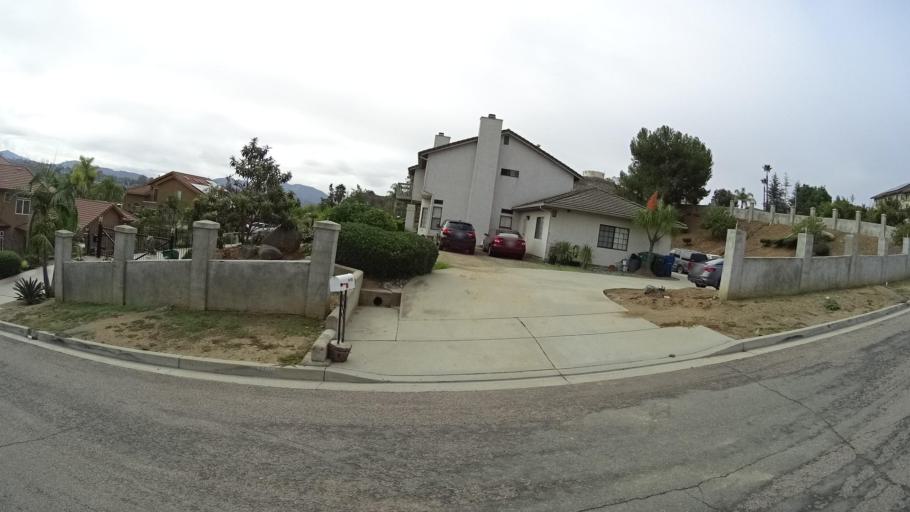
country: US
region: California
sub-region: San Diego County
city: Rancho San Diego
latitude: 32.7633
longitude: -116.9287
